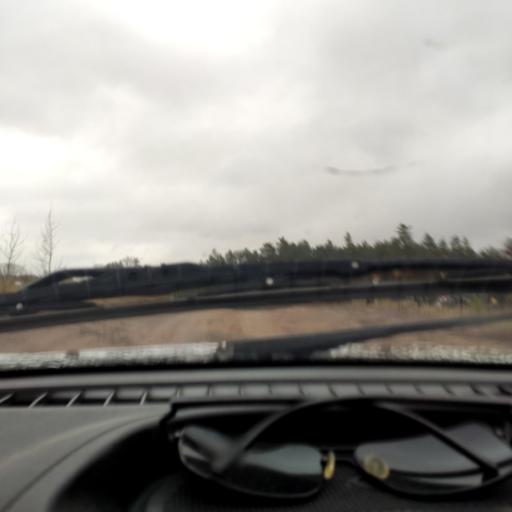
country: RU
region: Samara
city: Zhigulevsk
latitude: 53.5394
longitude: 49.5543
